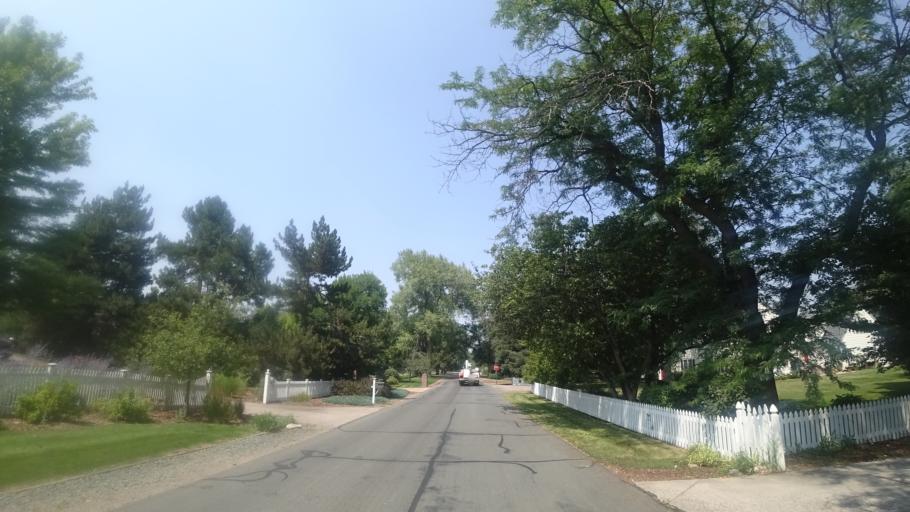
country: US
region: Colorado
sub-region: Arapahoe County
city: Cherry Hills Village
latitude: 39.6257
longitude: -104.9692
